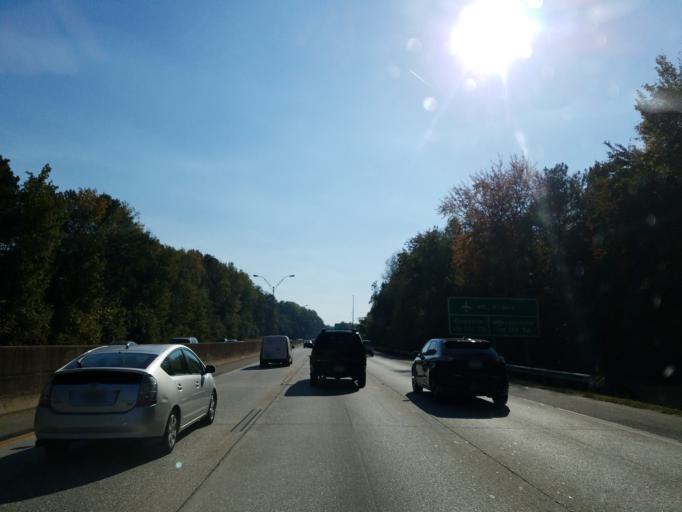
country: US
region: Georgia
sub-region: Fulton County
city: Hapeville
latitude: 33.6709
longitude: -84.4150
